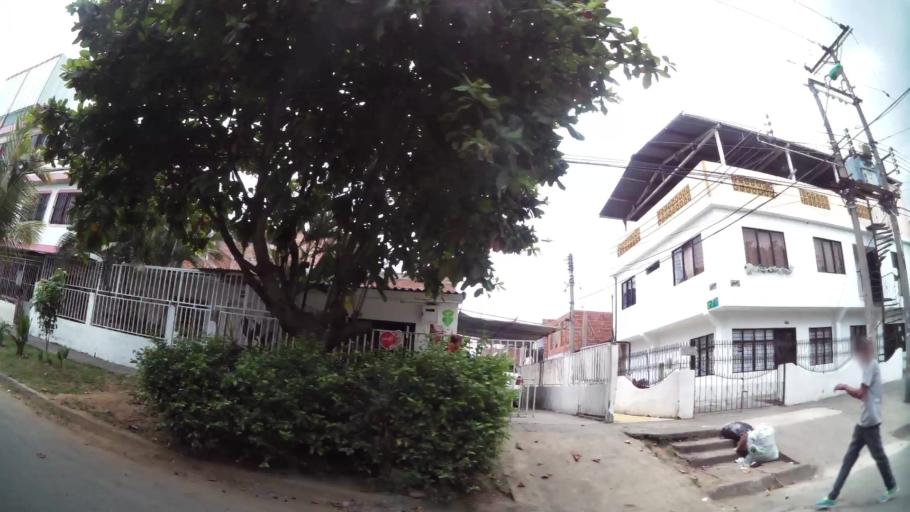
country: CO
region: Valle del Cauca
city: Cali
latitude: 3.4592
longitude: -76.4860
